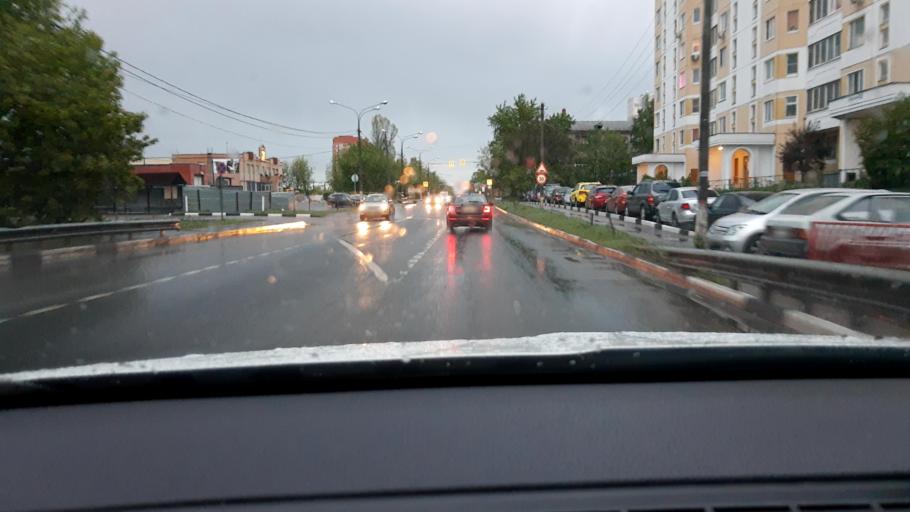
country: RU
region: Moskovskaya
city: Zagoryanskiy
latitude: 55.9275
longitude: 37.9563
